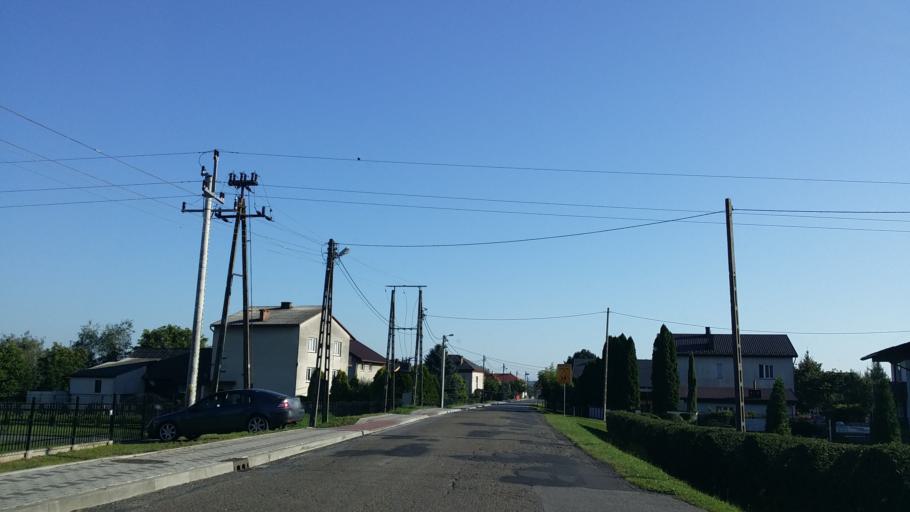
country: PL
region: Lesser Poland Voivodeship
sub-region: Powiat wadowicki
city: Spytkowice
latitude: 50.0224
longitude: 19.5085
